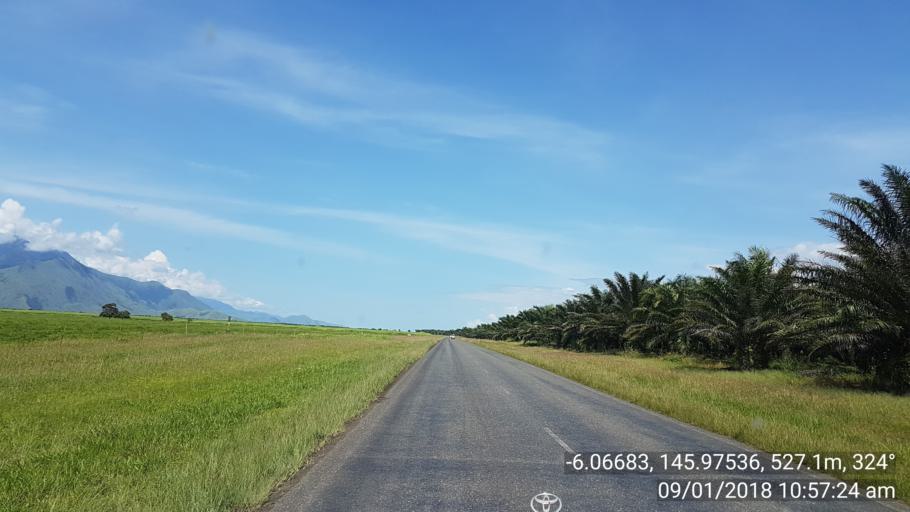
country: PG
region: Eastern Highlands
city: Kainantu
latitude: -6.0669
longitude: 145.9756
